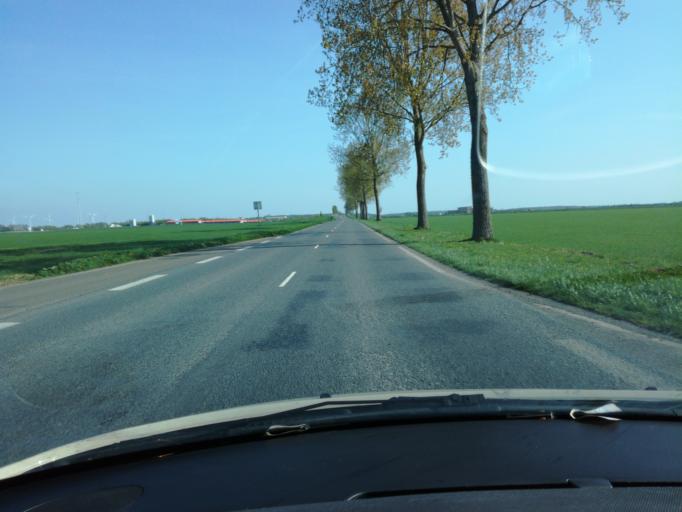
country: FR
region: Picardie
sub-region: Departement de la Somme
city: Poix-de-Picardie
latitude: 49.8144
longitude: 1.9615
